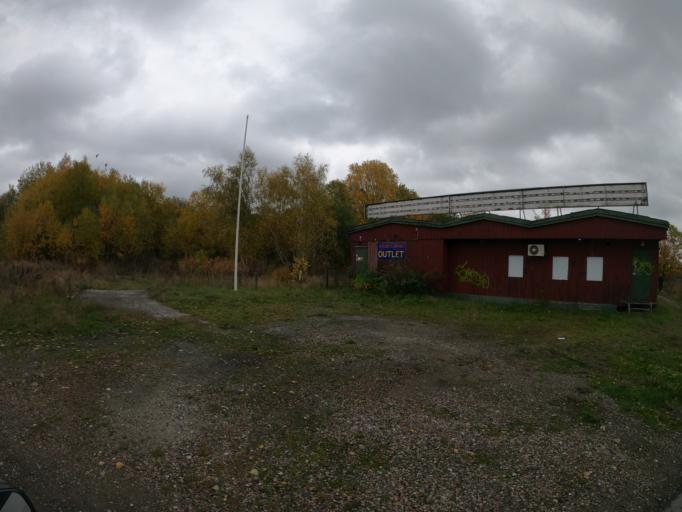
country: SE
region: Skane
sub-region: Lunds Kommun
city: Genarp
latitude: 55.6625
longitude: 13.3415
